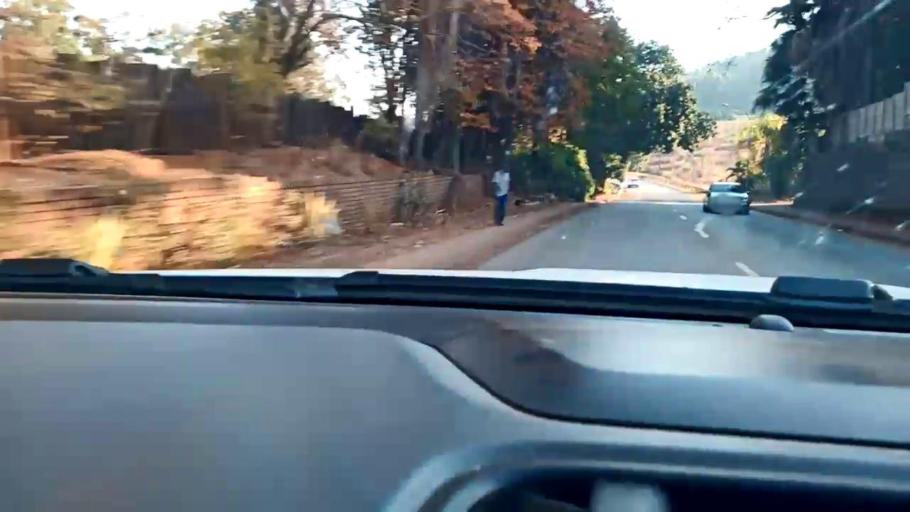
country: ZA
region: Limpopo
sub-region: Mopani District Municipality
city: Duiwelskloof
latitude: -23.6983
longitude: 30.1378
